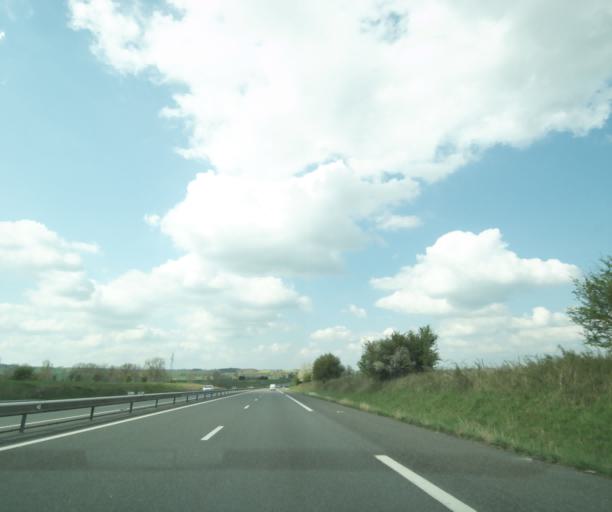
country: FR
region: Auvergne
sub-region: Departement de l'Allier
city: Bellenaves
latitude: 46.1998
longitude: 3.1030
